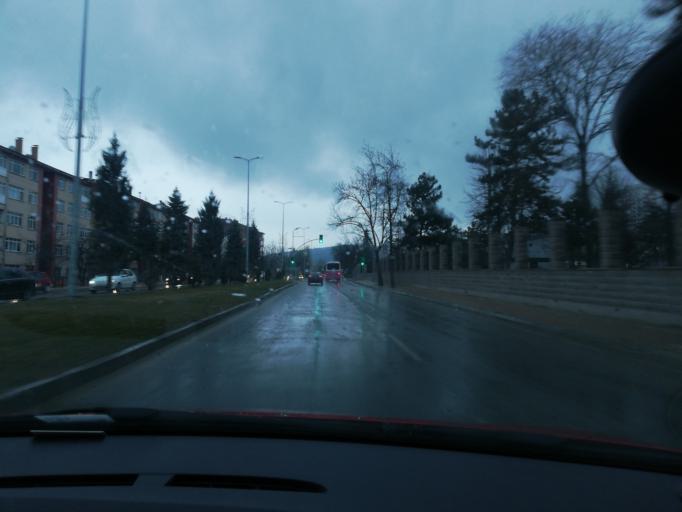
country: TR
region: Kastamonu
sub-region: Cide
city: Kastamonu
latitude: 41.4106
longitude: 33.7908
